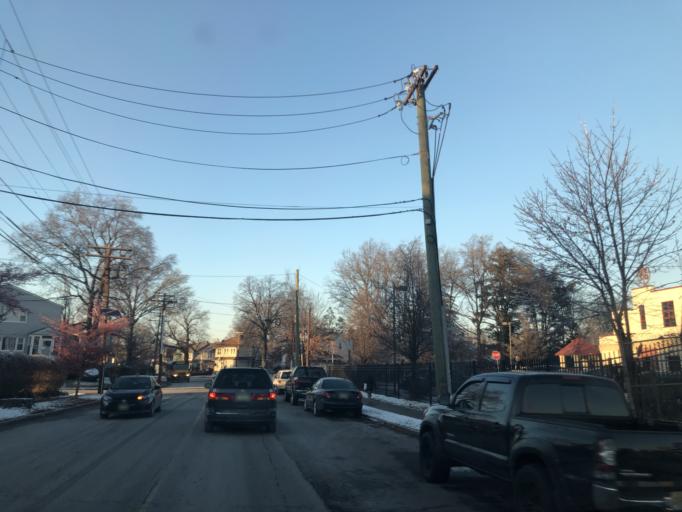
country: US
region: New Jersey
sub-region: Essex County
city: South Orange
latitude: 40.7368
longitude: -74.2512
